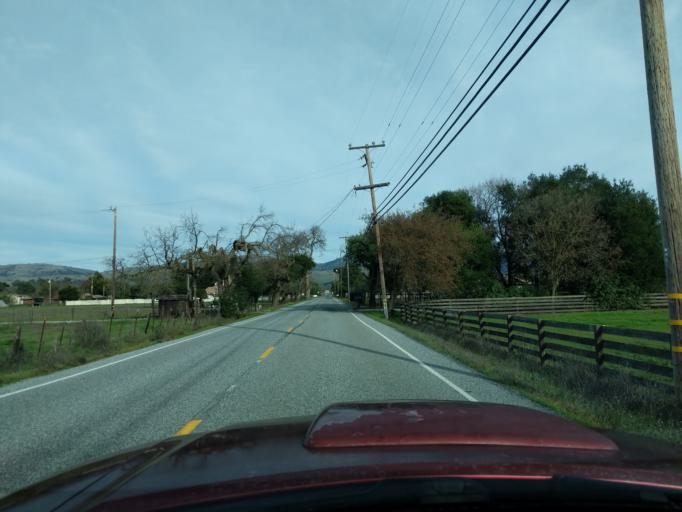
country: US
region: California
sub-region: Santa Clara County
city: San Martin
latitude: 37.0888
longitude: -121.6247
